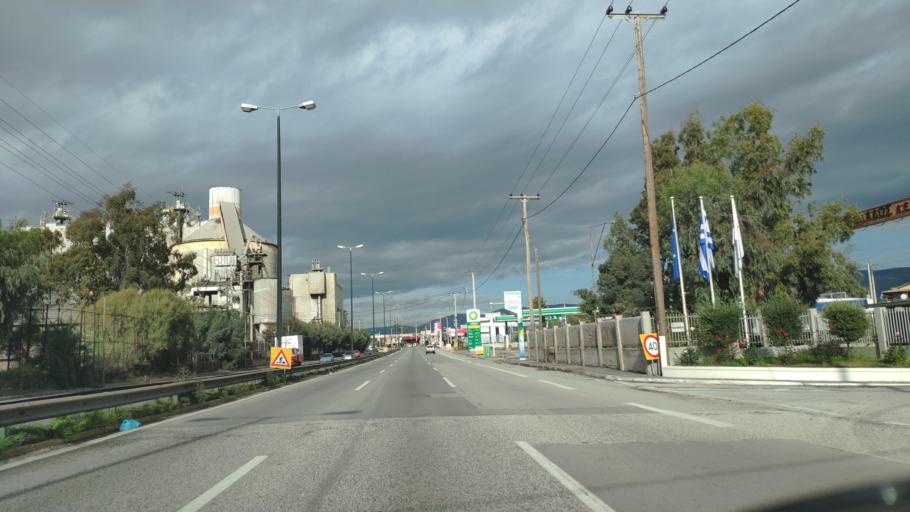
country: GR
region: Attica
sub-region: Nomarchia Athinas
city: Skaramangas
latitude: 38.0339
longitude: 23.5949
